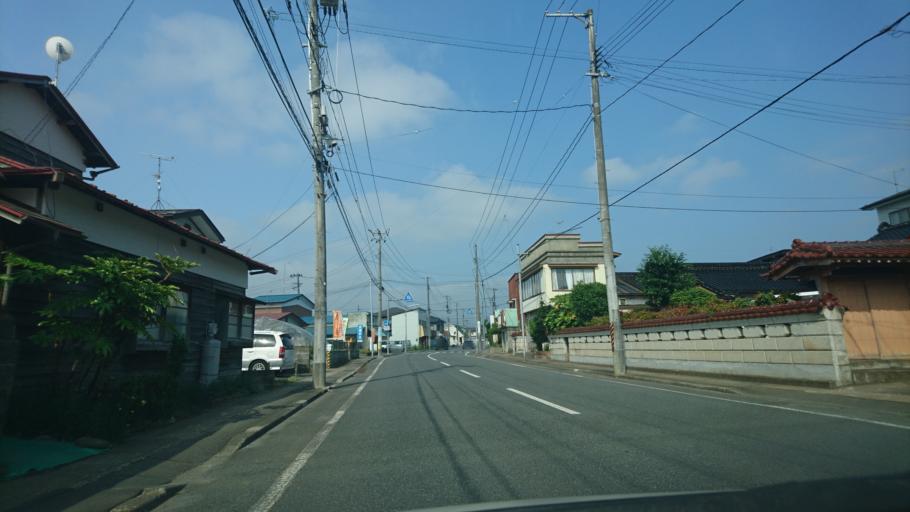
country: JP
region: Iwate
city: Ichinoseki
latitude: 38.9276
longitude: 141.1226
